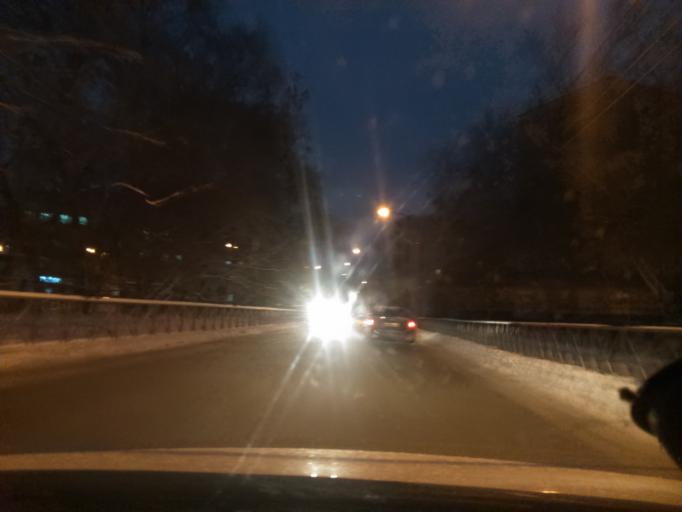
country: RU
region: Perm
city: Perm
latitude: 57.9876
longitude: 56.2427
